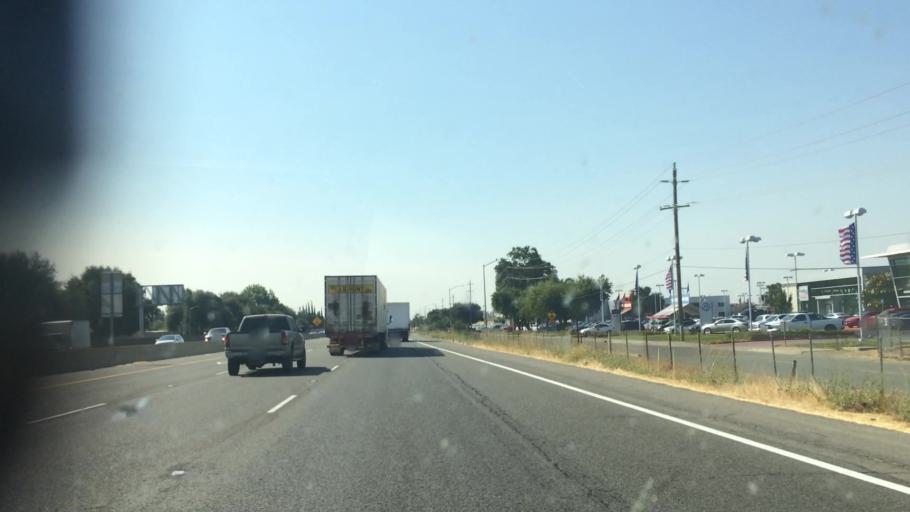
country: US
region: California
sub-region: Sacramento County
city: Elk Grove
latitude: 38.4047
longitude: -121.3861
